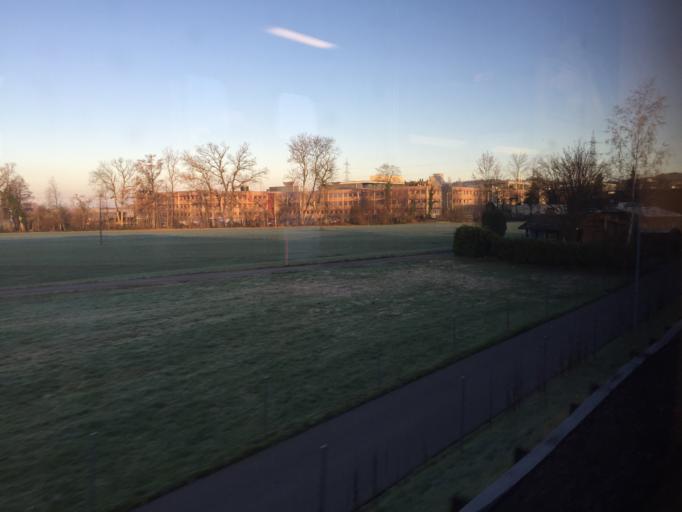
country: CH
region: Zug
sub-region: Zug
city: Zug
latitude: 47.1849
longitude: 8.5172
